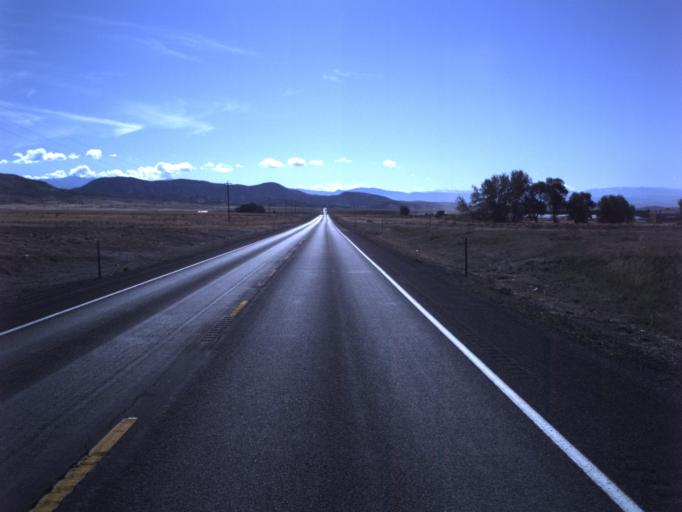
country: US
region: Utah
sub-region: Sanpete County
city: Gunnison
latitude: 39.2697
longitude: -111.8715
